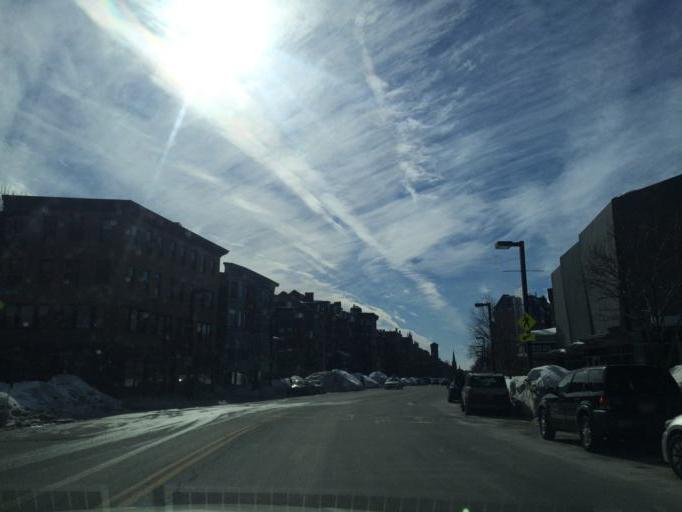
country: US
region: Massachusetts
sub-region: Suffolk County
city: Boston
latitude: 42.3449
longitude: -71.0702
